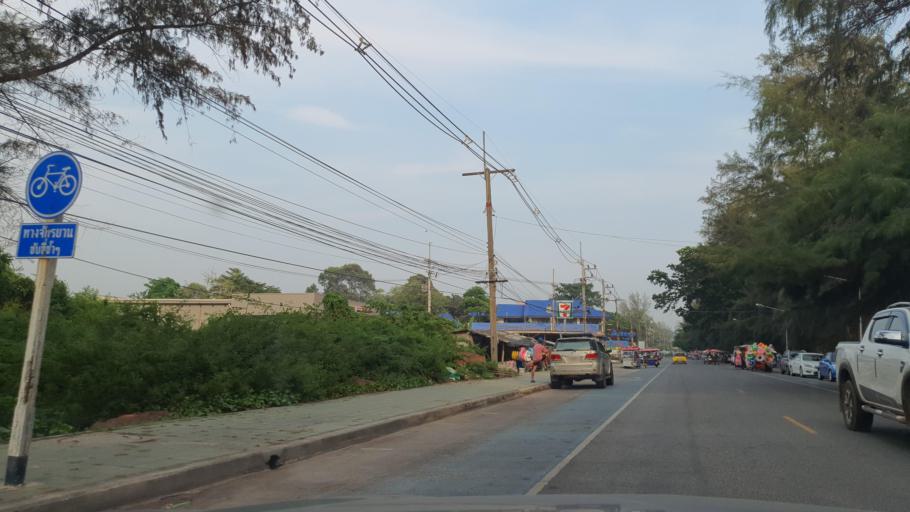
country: TH
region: Rayong
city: Rayong
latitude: 12.5992
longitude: 101.4061
